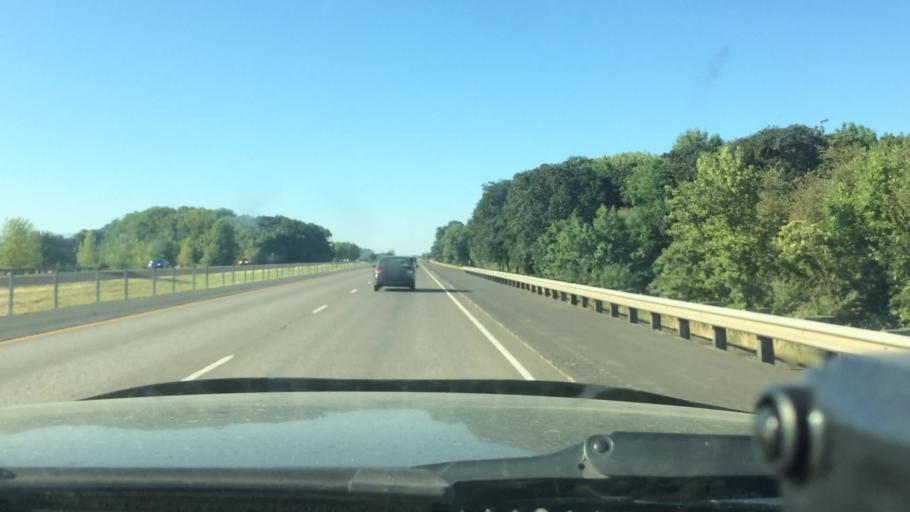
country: US
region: Oregon
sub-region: Linn County
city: Tangent
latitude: 44.4776
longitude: -123.0617
